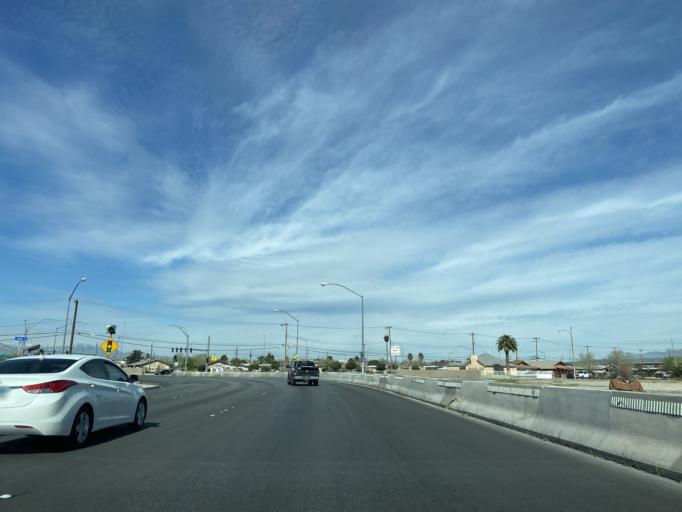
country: US
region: Nevada
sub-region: Clark County
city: North Las Vegas
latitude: 36.1966
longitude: -115.1323
